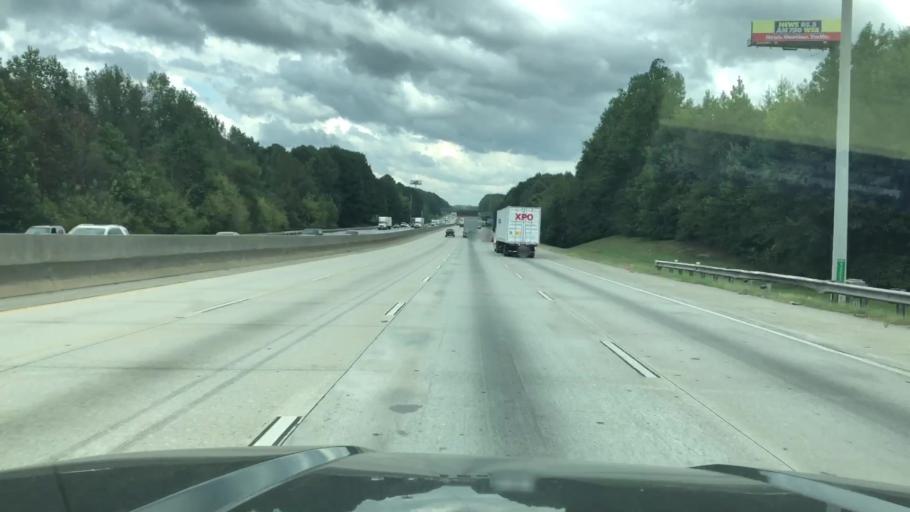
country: US
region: Georgia
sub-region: Fulton County
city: Fairburn
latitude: 33.5514
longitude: -84.5647
